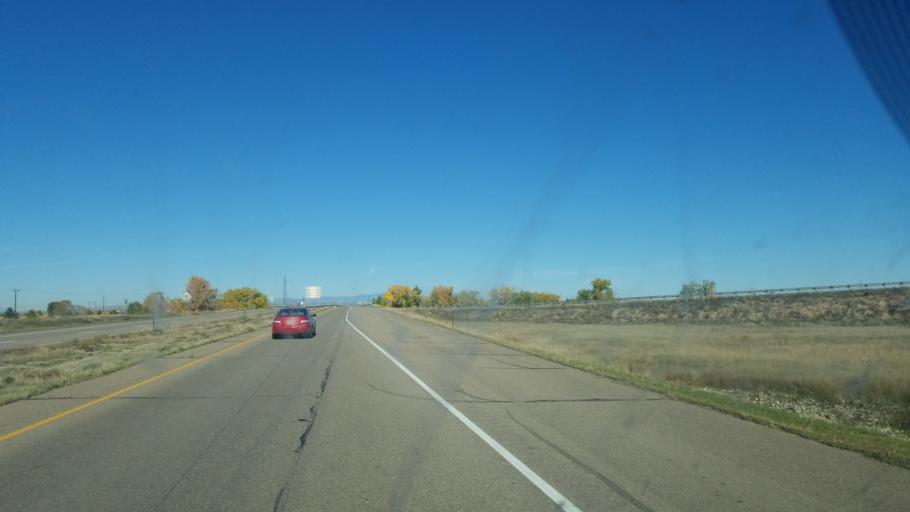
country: US
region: Colorado
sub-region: Pueblo County
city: Pueblo
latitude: 38.2637
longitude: -104.3701
